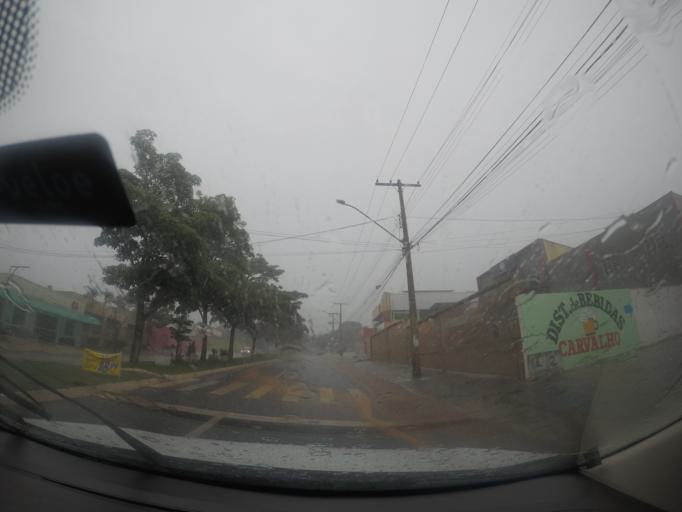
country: BR
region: Goias
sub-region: Goiania
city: Goiania
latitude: -16.6065
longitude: -49.3371
